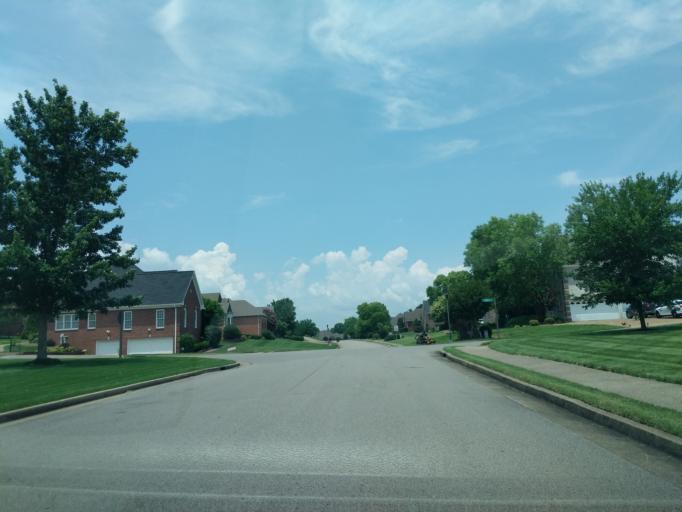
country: US
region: Tennessee
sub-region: Davidson County
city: Lakewood
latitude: 36.2302
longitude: -86.6297
